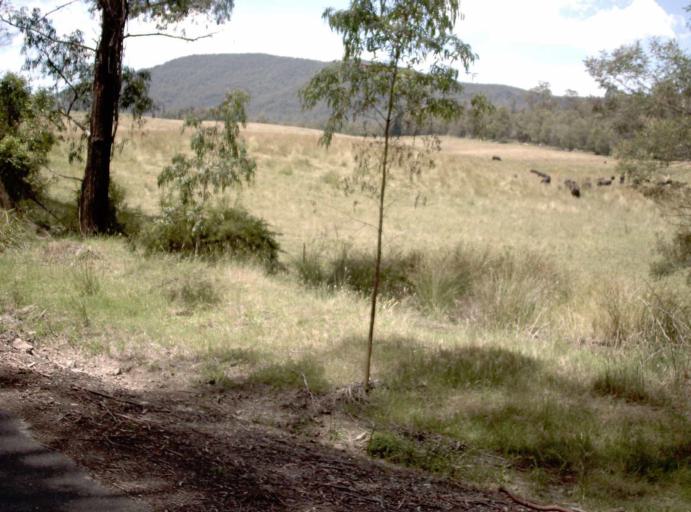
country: AU
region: New South Wales
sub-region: Bombala
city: Bombala
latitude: -37.4261
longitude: 149.0085
